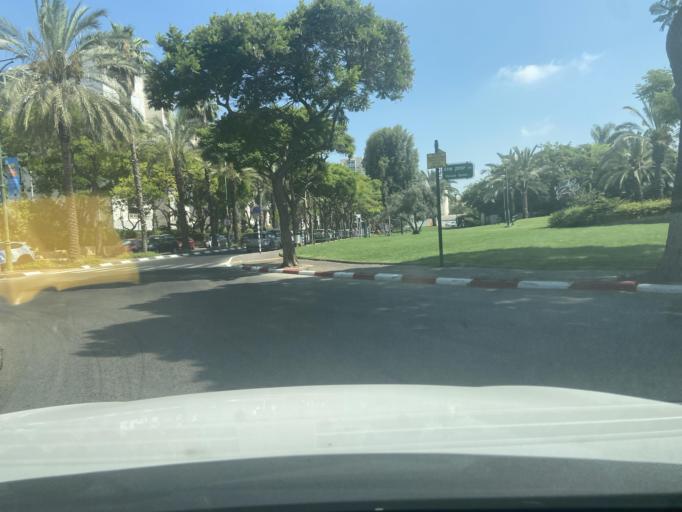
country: IL
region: Central District
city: Yehud
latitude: 32.0302
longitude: 34.8810
